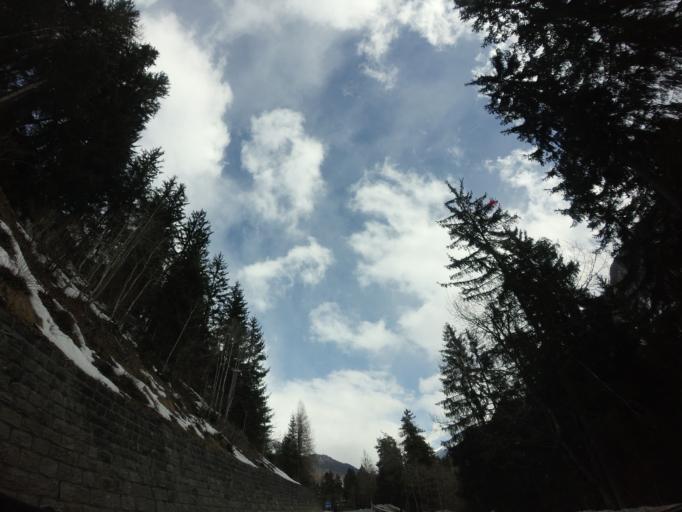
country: AT
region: Tyrol
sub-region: Politischer Bezirk Landeck
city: Nauders
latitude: 46.8520
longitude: 10.4212
